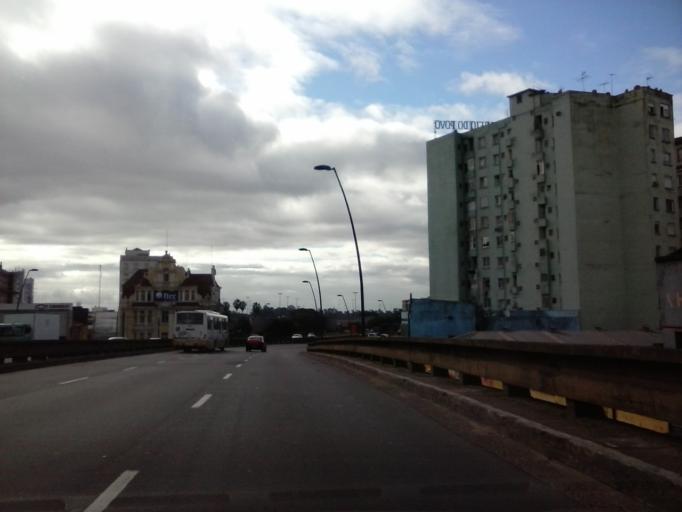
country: BR
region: Rio Grande do Sul
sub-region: Porto Alegre
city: Porto Alegre
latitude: -30.0276
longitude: -51.2195
